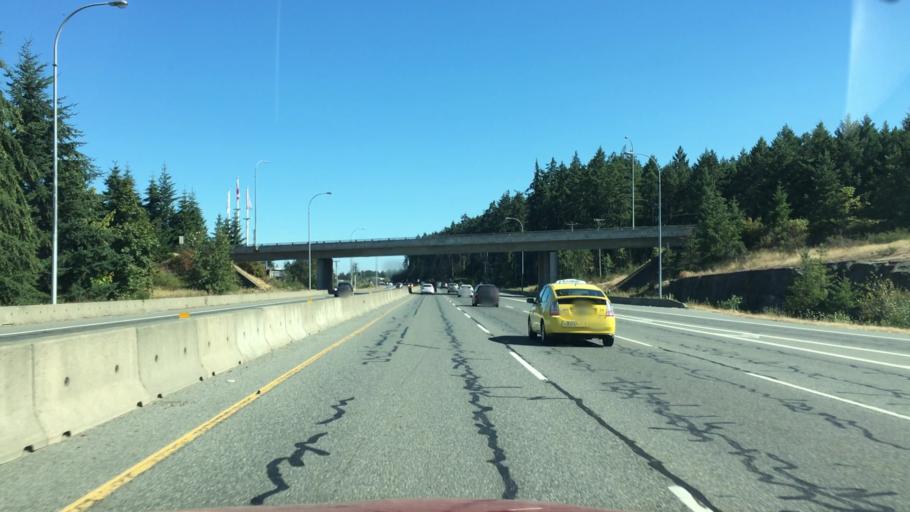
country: CA
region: British Columbia
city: Nanaimo
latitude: 49.1111
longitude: -123.9028
